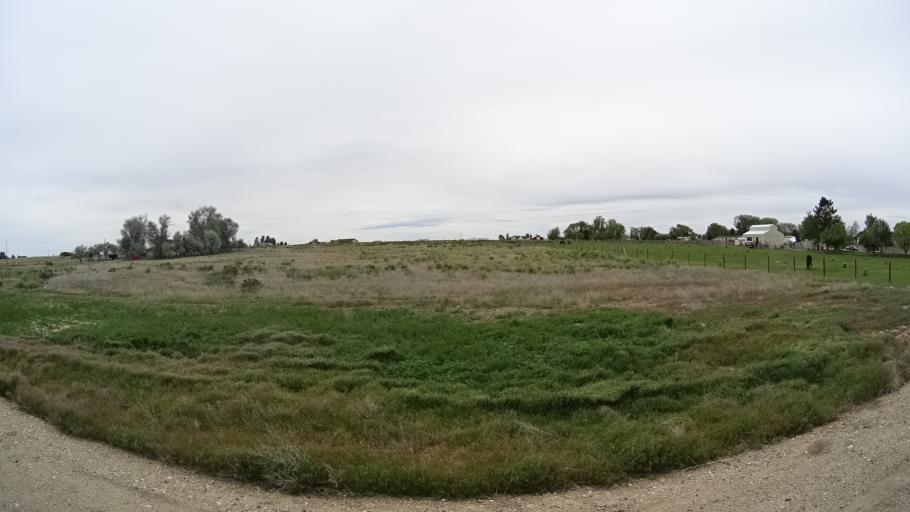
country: US
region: Idaho
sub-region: Ada County
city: Kuna
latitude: 43.4884
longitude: -116.3117
